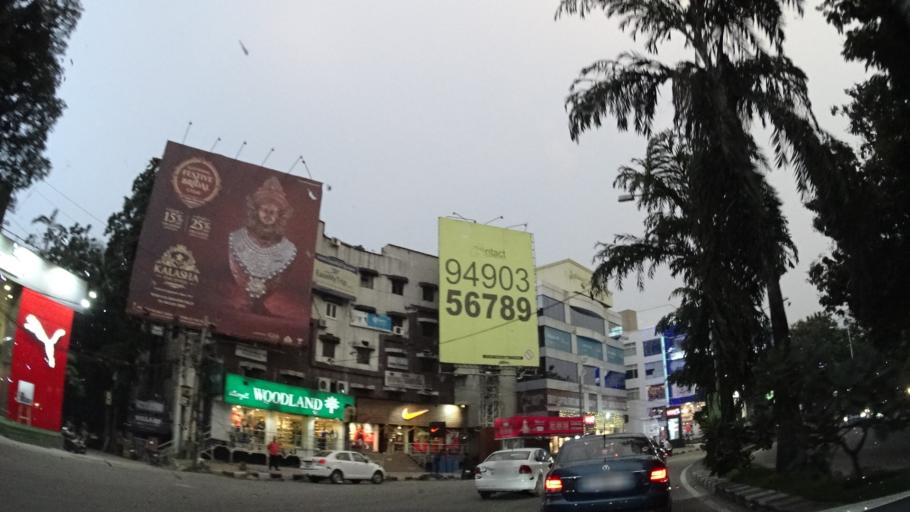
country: IN
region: Telangana
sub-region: Hyderabad
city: Hyderabad
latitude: 17.4226
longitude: 78.4495
